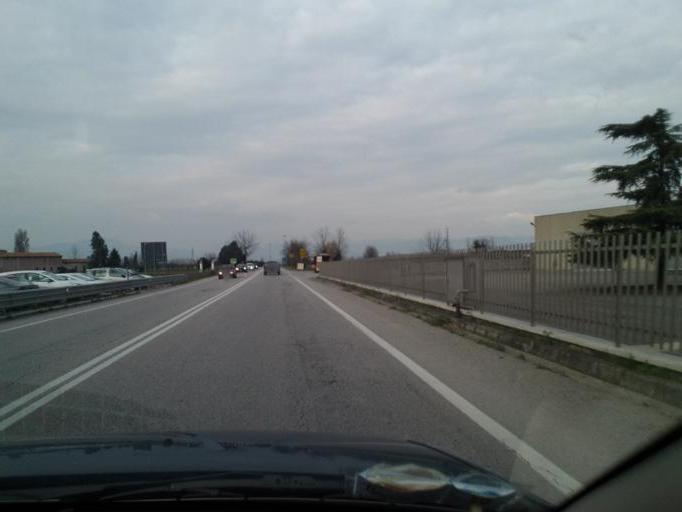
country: IT
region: Veneto
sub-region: Provincia di Verona
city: Sona
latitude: 45.4339
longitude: 10.8483
